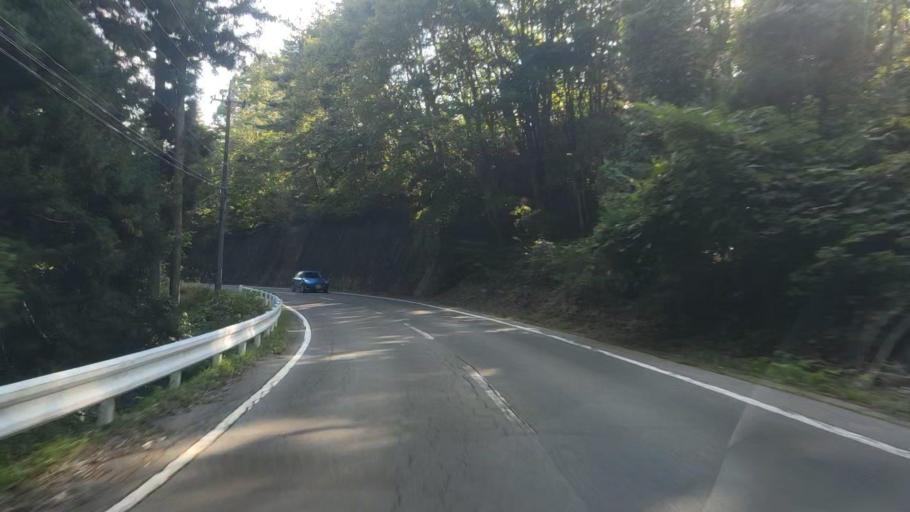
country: JP
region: Nagano
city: Suzaka
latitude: 36.5480
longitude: 138.5570
